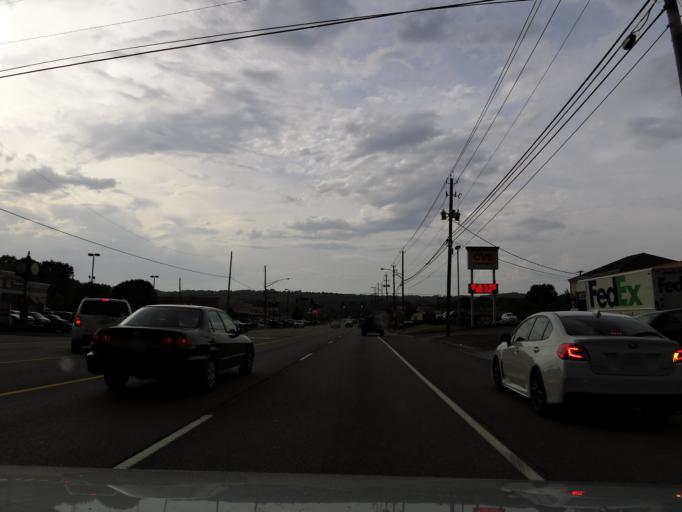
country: US
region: Tennessee
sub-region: Knox County
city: Knoxville
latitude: 36.0275
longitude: -83.9278
